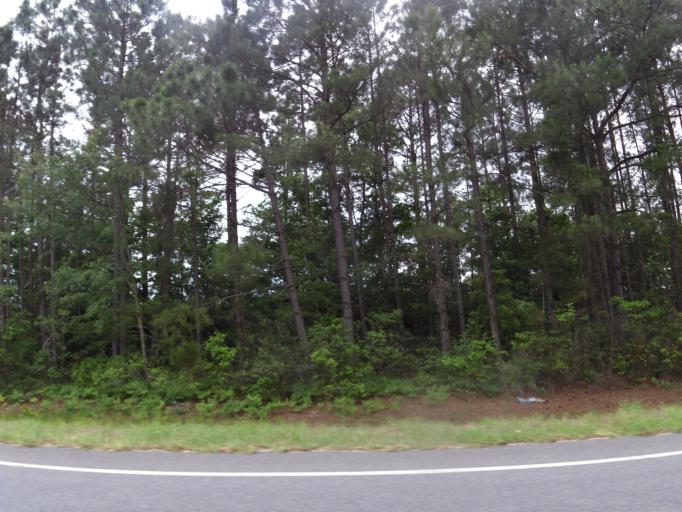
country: US
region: Georgia
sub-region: Candler County
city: Metter
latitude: 32.3996
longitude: -82.1852
